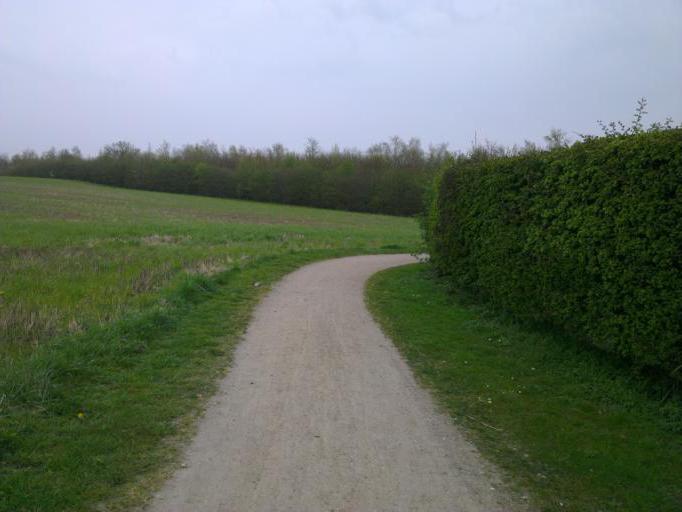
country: DK
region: Capital Region
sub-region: Frederikssund Kommune
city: Frederikssund
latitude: 55.8397
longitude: 12.0822
